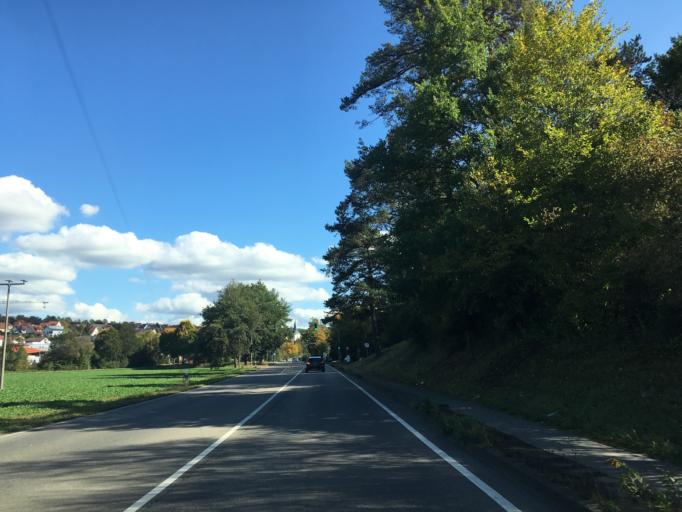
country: DE
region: Baden-Wuerttemberg
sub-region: Regierungsbezirk Stuttgart
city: Aidlingen
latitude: 48.7146
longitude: 8.9017
